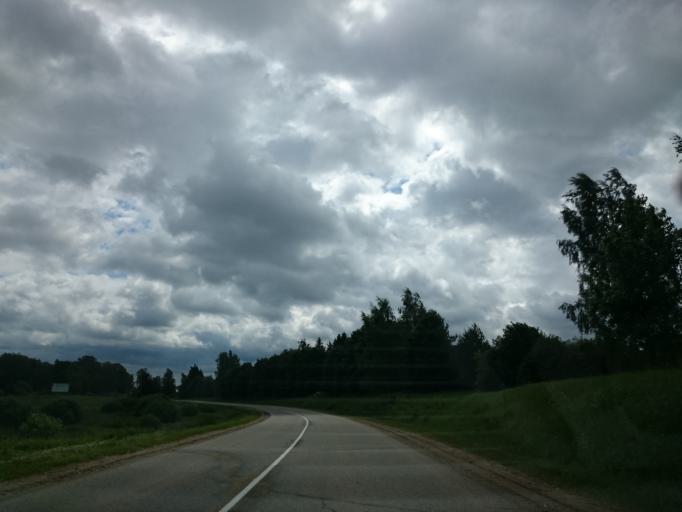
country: LV
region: Madonas Rajons
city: Madona
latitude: 56.8611
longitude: 26.1871
